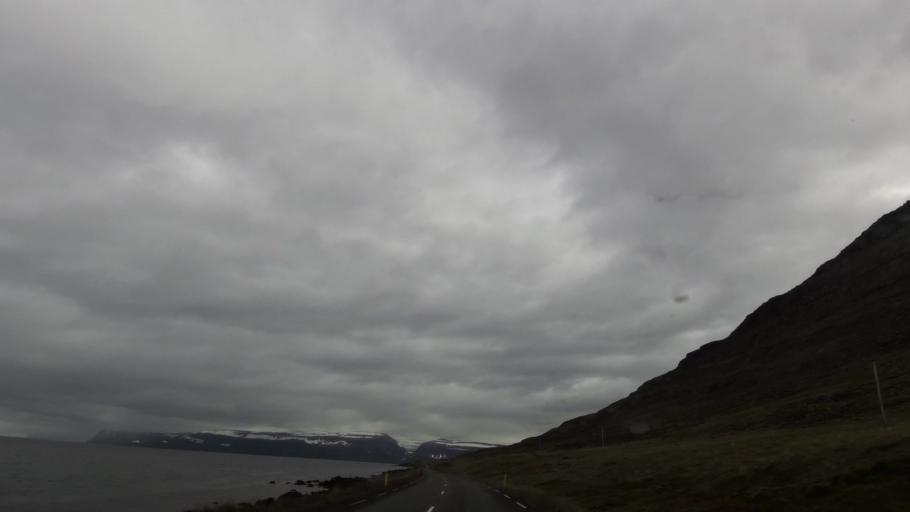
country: IS
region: Westfjords
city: Isafjoerdur
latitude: 66.0307
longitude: -22.7750
